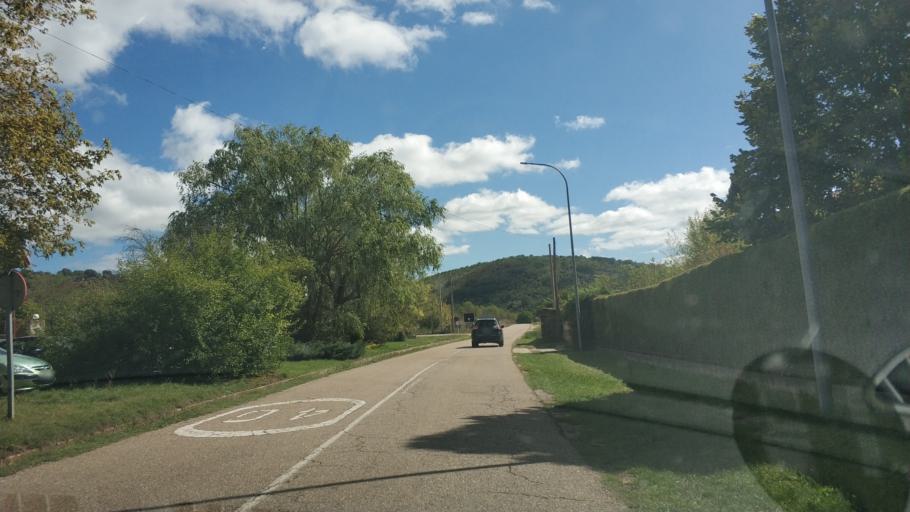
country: ES
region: Castille and Leon
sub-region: Provincia de Burgos
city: Covarrubias
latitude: 42.0590
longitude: -3.5141
